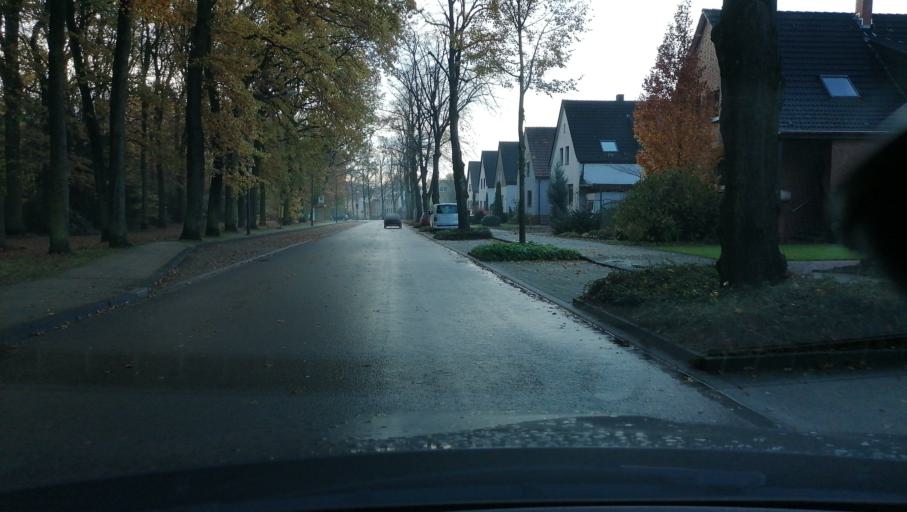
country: DE
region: North Rhine-Westphalia
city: Herten
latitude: 51.5904
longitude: 7.1514
